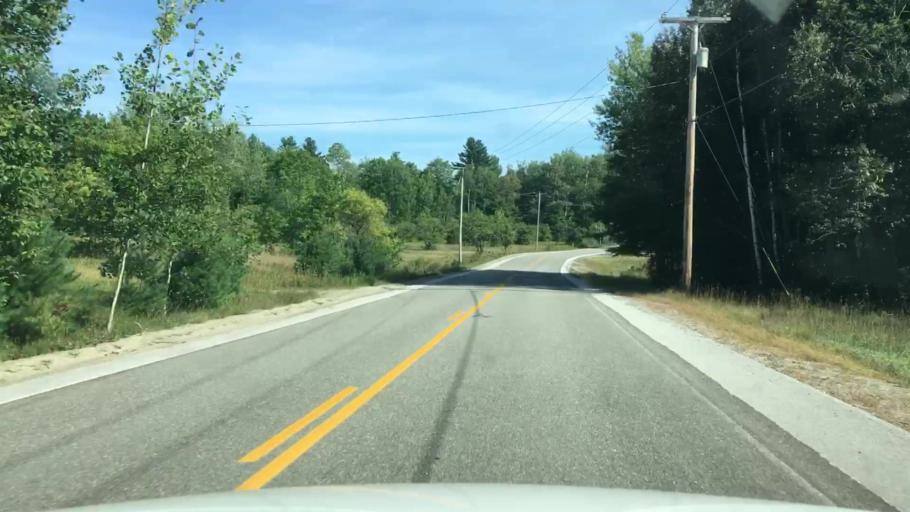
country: US
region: Maine
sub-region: Penobscot County
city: Enfield
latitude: 45.2145
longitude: -68.5277
